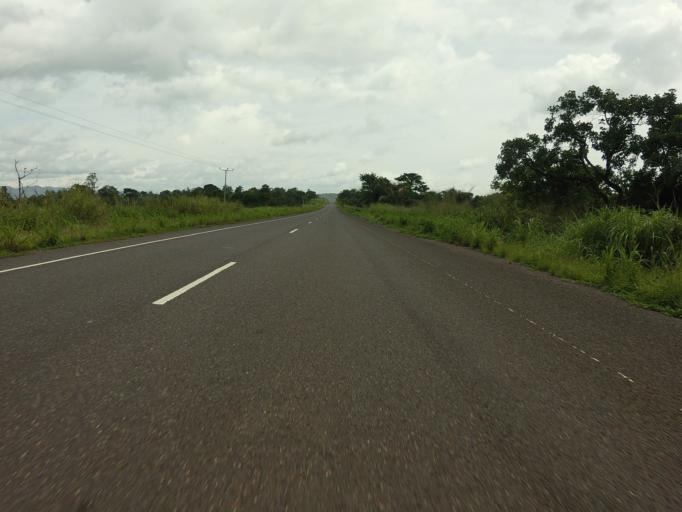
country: TG
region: Plateaux
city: Badou
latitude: 7.9735
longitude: 0.5590
